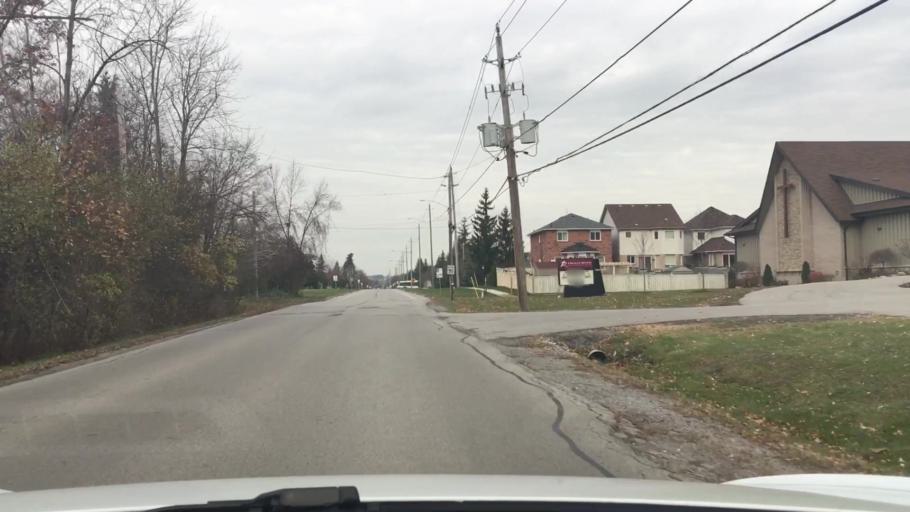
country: CA
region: Ontario
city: Oshawa
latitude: 43.9004
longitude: -78.7836
